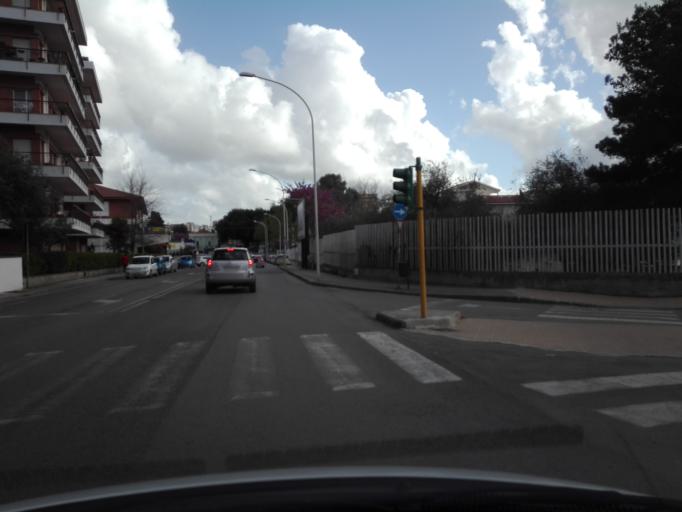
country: IT
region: Sardinia
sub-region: Provincia di Sassari
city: Sassari
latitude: 40.7207
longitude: 8.5781
